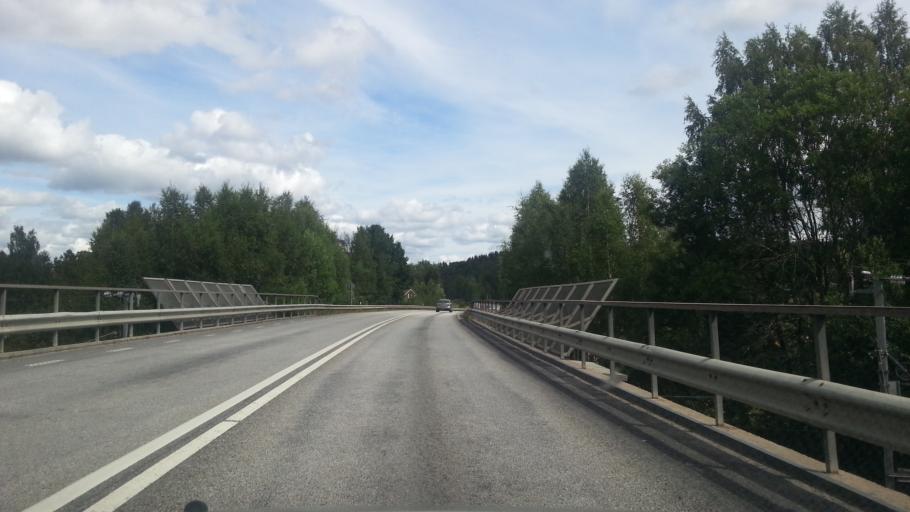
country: SE
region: OErebro
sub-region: Lindesbergs Kommun
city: Lindesberg
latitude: 59.6372
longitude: 15.2210
